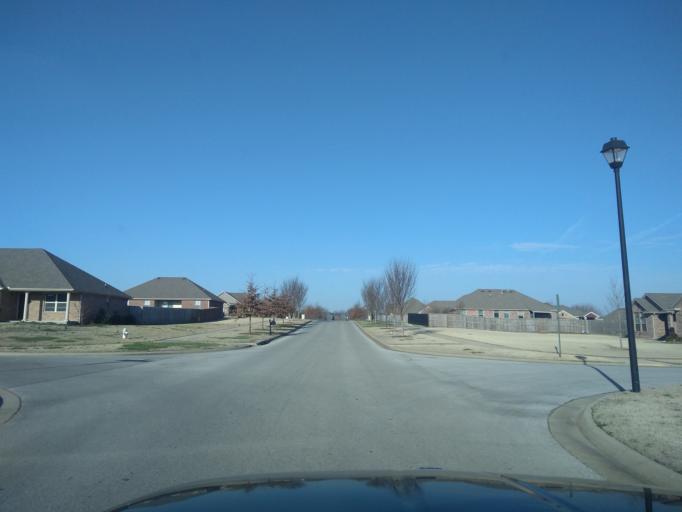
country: US
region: Arkansas
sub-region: Washington County
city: Farmington
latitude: 36.0710
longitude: -94.2470
